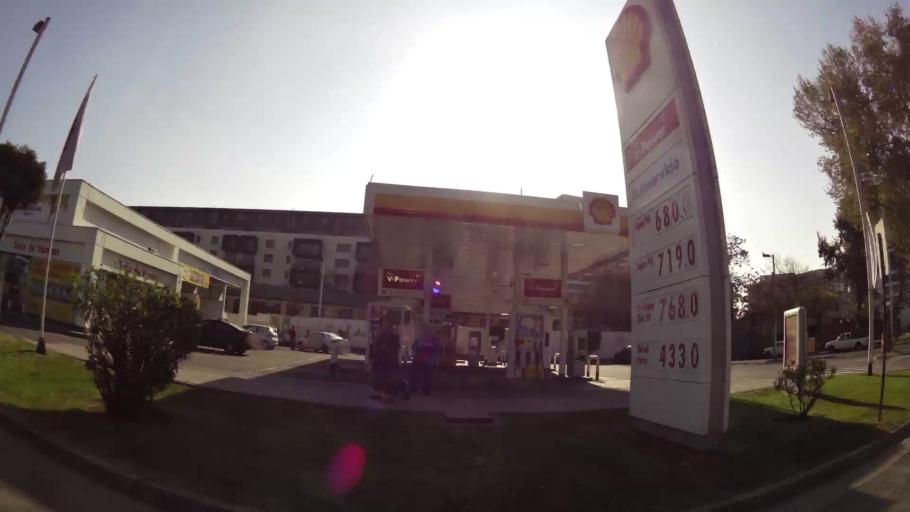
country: CL
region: Santiago Metropolitan
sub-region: Provincia de Santiago
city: Villa Presidente Frei, Nunoa, Santiago, Chile
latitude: -33.4581
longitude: -70.5722
